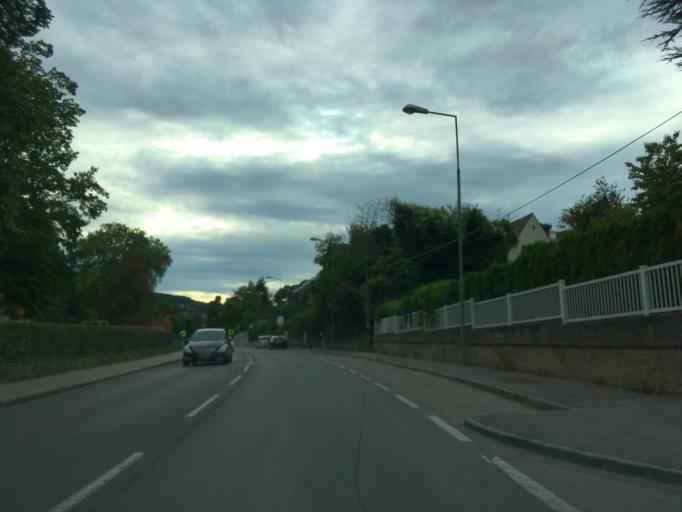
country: AT
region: Lower Austria
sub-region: Politischer Bezirk Wien-Umgebung
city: Klosterneuburg
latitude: 48.3061
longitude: 16.2979
